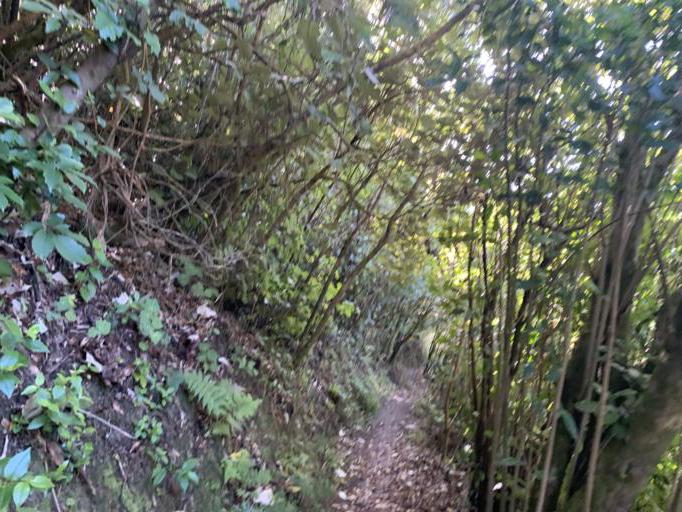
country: NZ
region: Wellington
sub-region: Wellington City
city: Brooklyn
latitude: -41.2999
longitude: 174.7541
